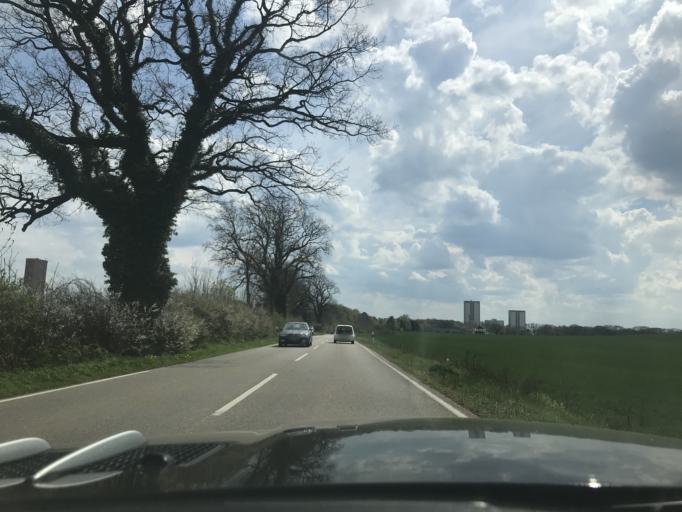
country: DE
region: Schleswig-Holstein
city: Sierksdorf
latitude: 54.0810
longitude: 10.7765
